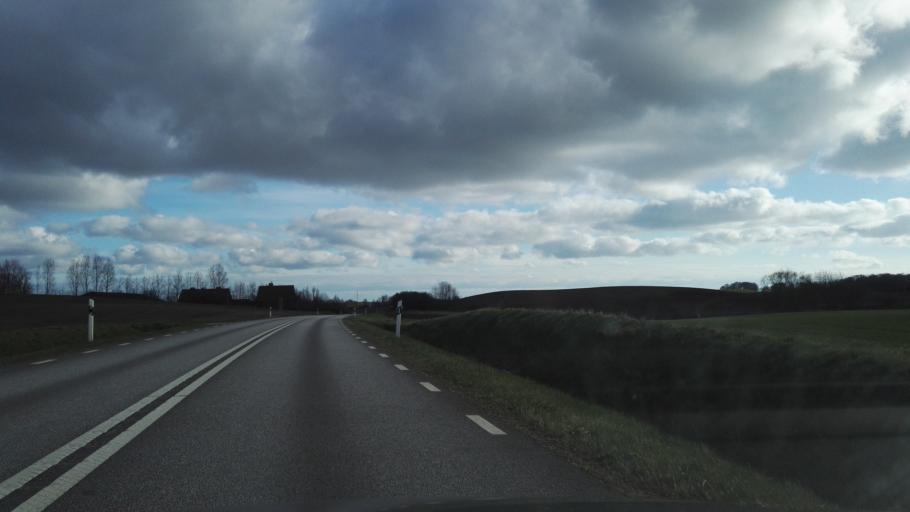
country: SE
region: Skane
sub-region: Ystads Kommun
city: Ystad
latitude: 55.4632
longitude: 13.7987
